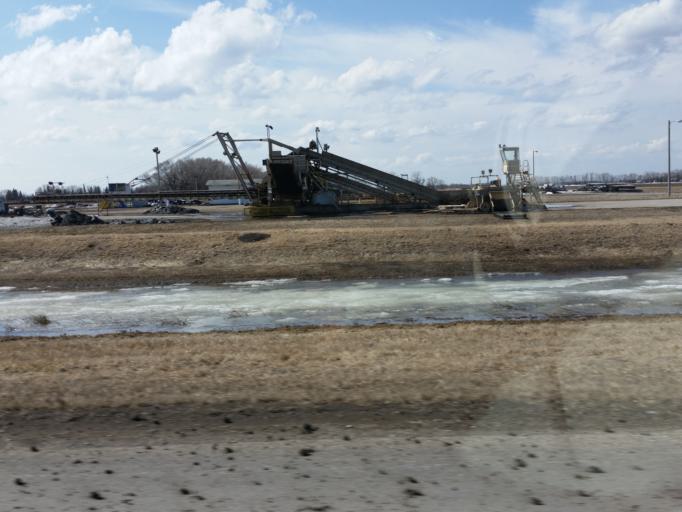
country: US
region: North Dakota
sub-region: Walsh County
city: Grafton
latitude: 48.2169
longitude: -97.3625
